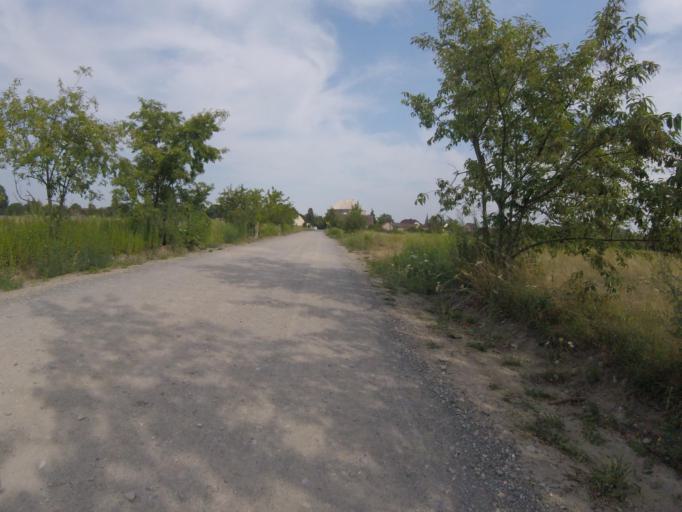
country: DE
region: Brandenburg
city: Spreenhagen
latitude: 52.3002
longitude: 13.7835
